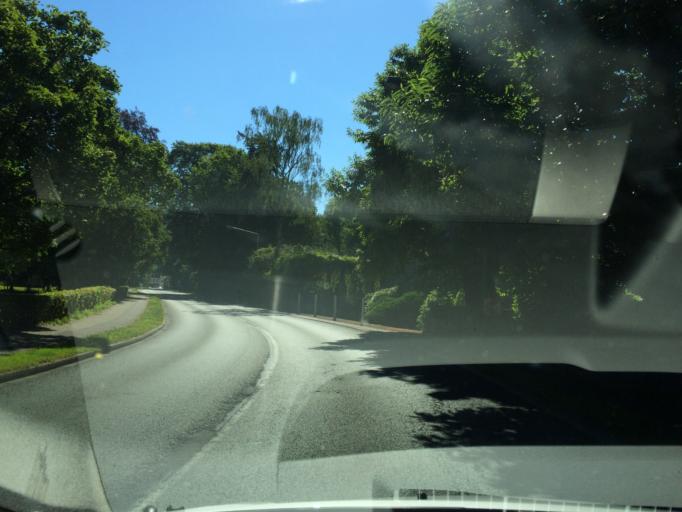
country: DE
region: North Rhine-Westphalia
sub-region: Regierungsbezirk Arnsberg
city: Nachrodt-Wiblingwerde
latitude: 51.3356
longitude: 7.6358
